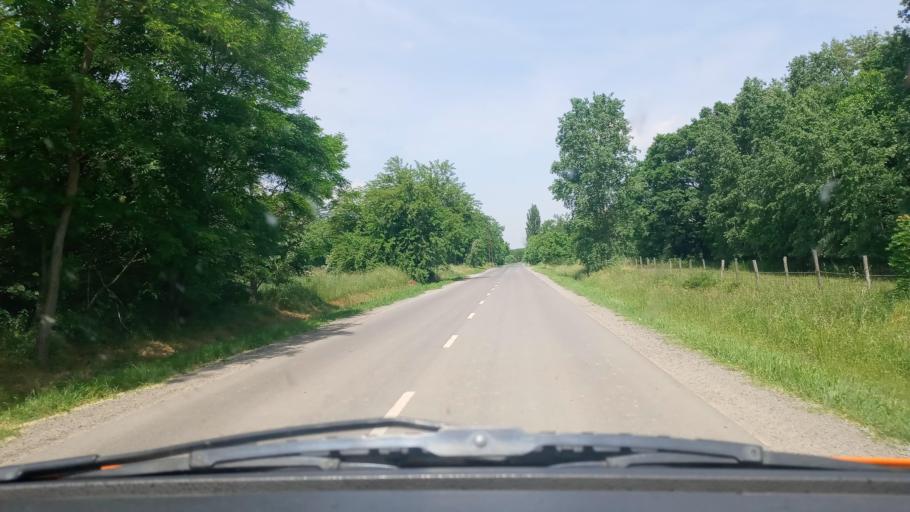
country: HU
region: Baranya
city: Szigetvar
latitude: 45.9679
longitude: 17.7225
